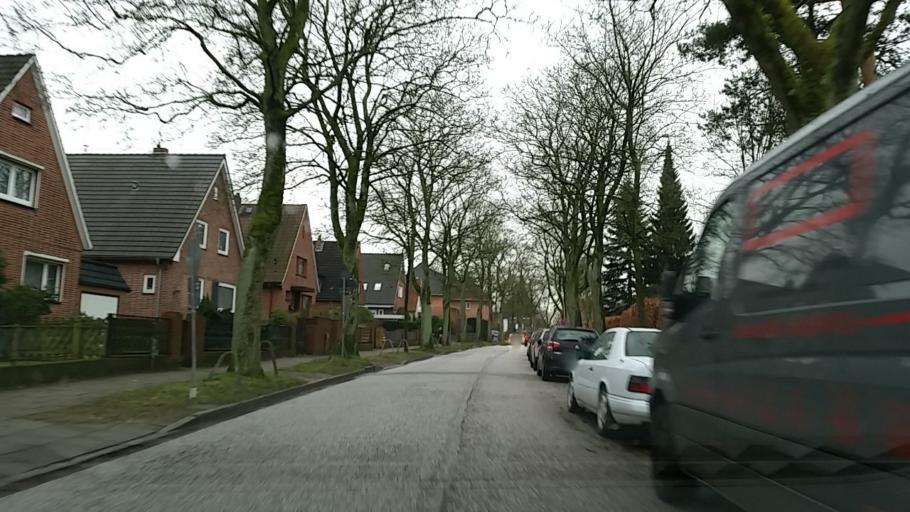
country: DE
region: Hamburg
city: Bergedorf
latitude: 53.4826
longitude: 10.2336
